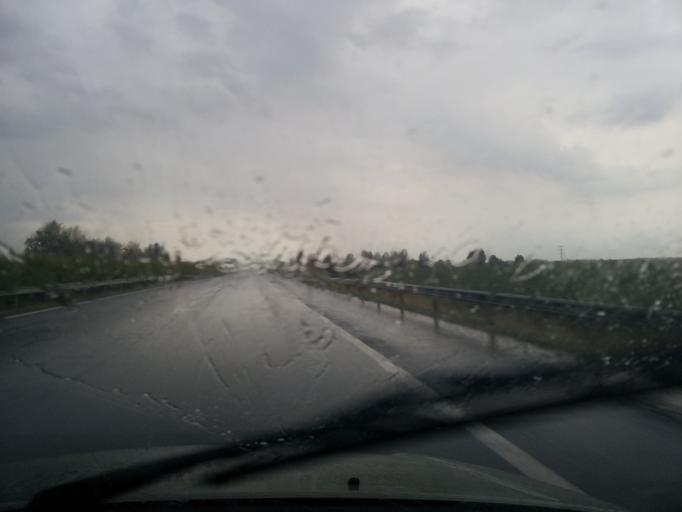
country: HU
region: Borsod-Abauj-Zemplen
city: Malyi
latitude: 48.0166
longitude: 20.8737
